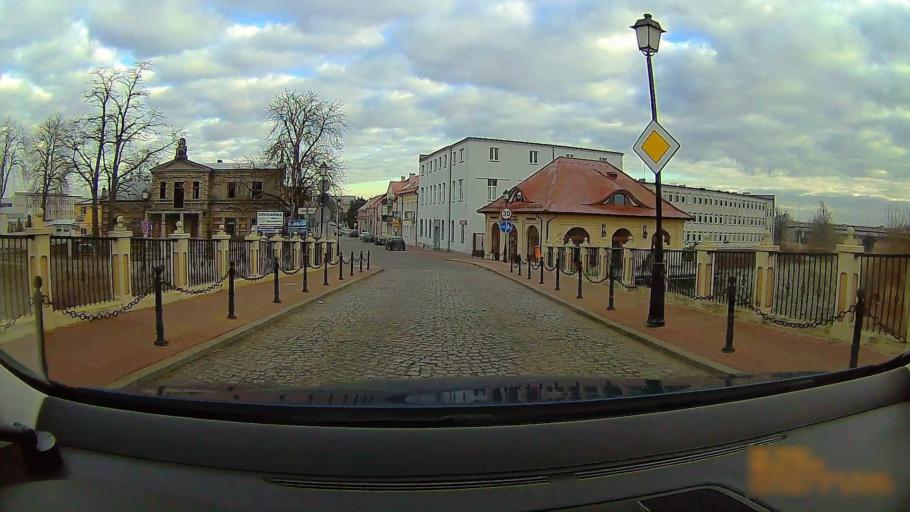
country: PL
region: Greater Poland Voivodeship
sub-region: Konin
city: Konin
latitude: 52.2133
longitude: 18.2549
